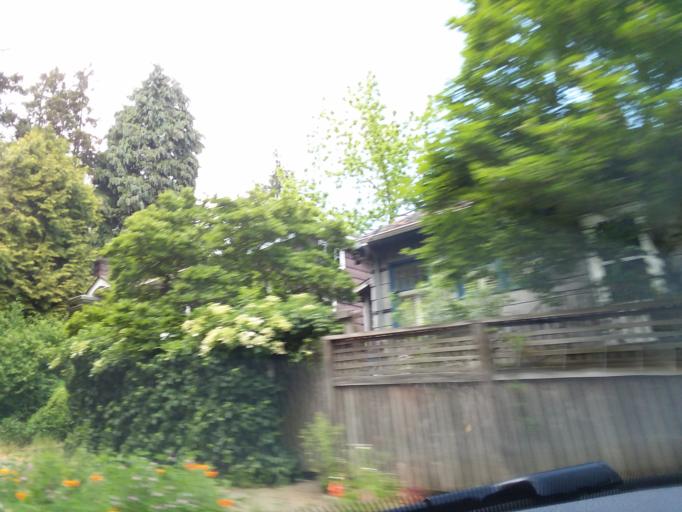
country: US
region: Washington
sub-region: King County
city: Seattle
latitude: 47.6556
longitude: -122.3321
